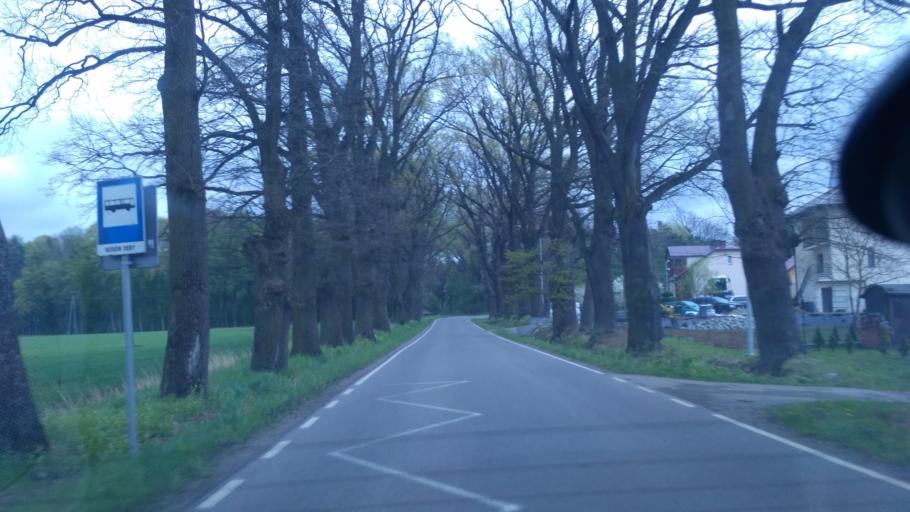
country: PL
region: Subcarpathian Voivodeship
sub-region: Powiat brzozowski
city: Turze Pole
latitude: 49.6461
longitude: 21.9968
